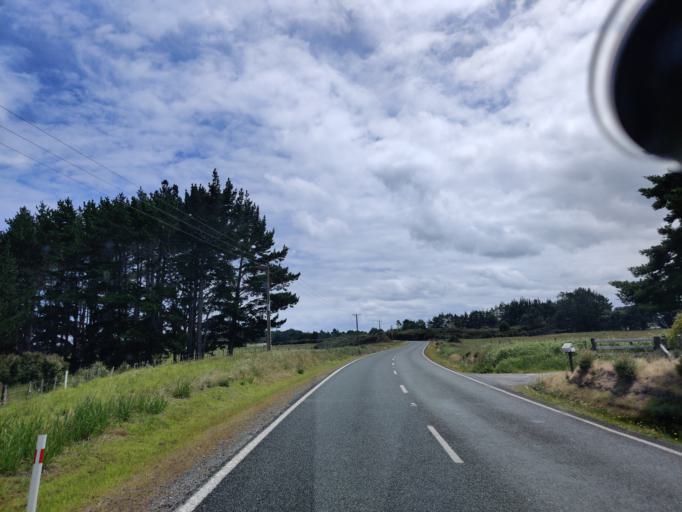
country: NZ
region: Northland
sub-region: Far North District
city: Kaitaia
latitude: -34.6673
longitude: 172.9751
